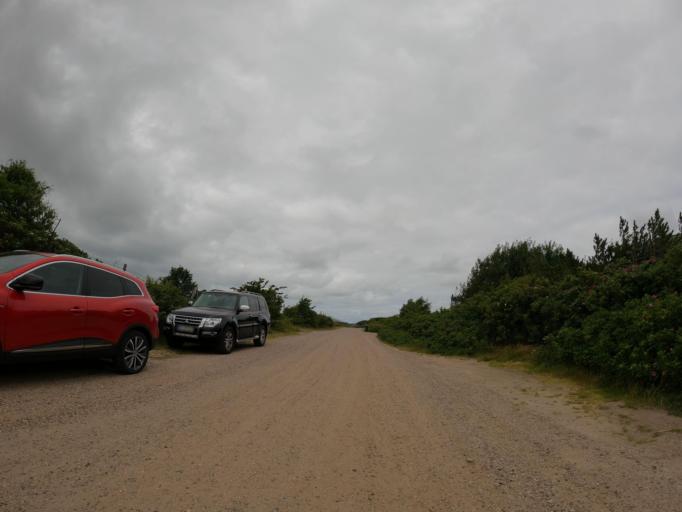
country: DE
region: Schleswig-Holstein
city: Tinnum
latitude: 54.9164
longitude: 8.3549
